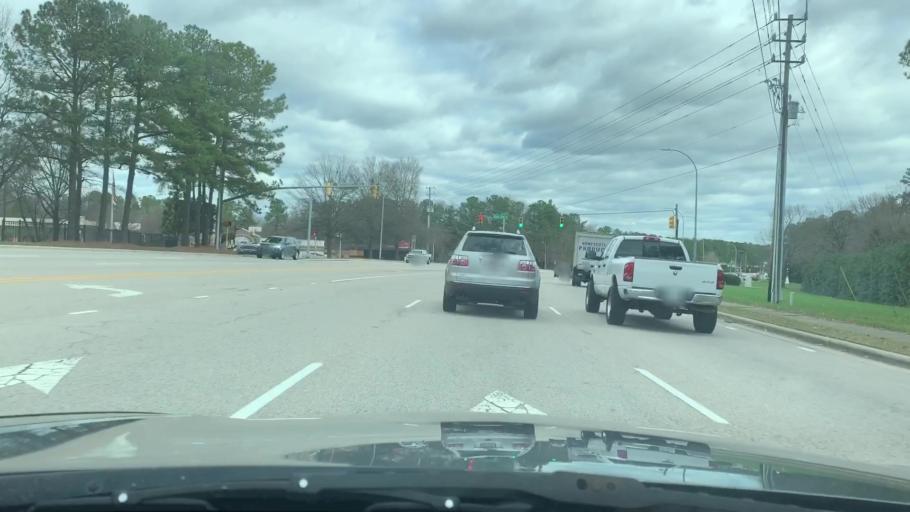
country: US
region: North Carolina
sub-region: Wake County
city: Cary
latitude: 35.8292
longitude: -78.7690
